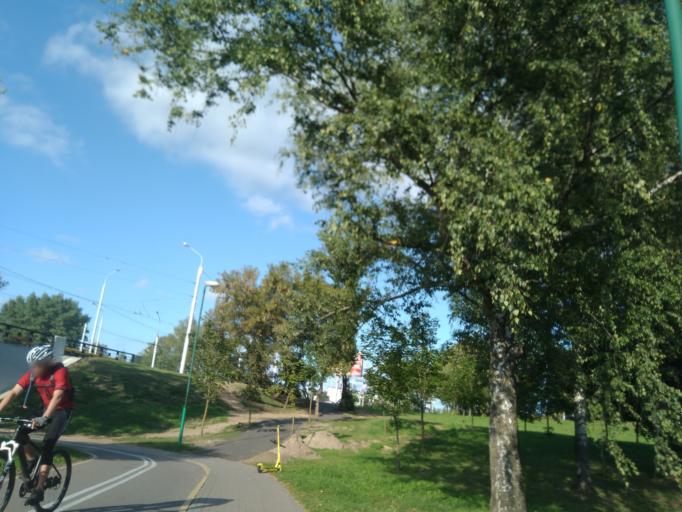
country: BY
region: Minsk
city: Minsk
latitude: 53.8737
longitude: 27.5843
